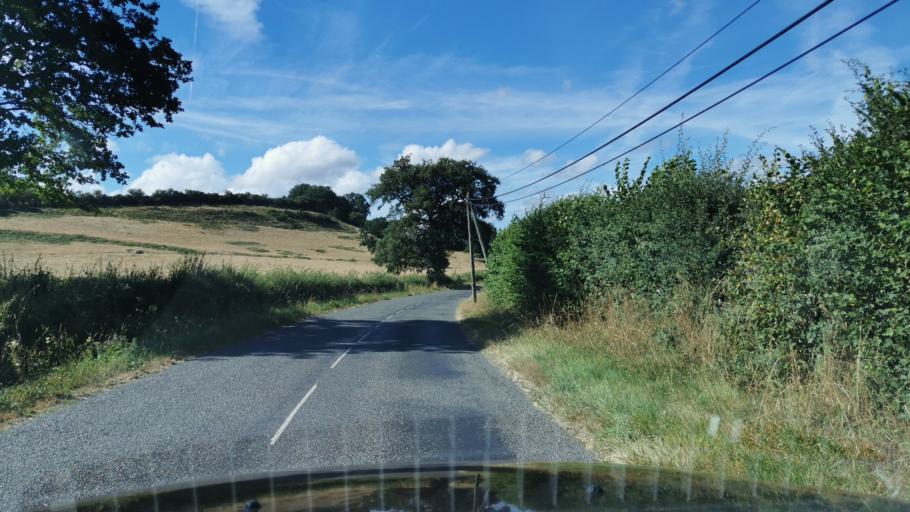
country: FR
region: Bourgogne
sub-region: Departement de Saone-et-Loire
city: Marmagne
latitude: 46.8062
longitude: 4.3282
